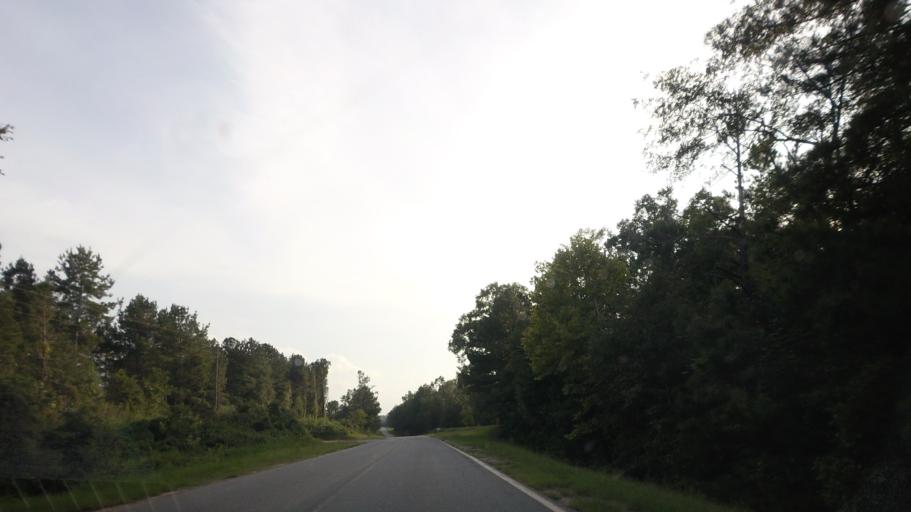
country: US
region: Georgia
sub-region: Wilkinson County
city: Gordon
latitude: 32.8452
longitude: -83.3540
